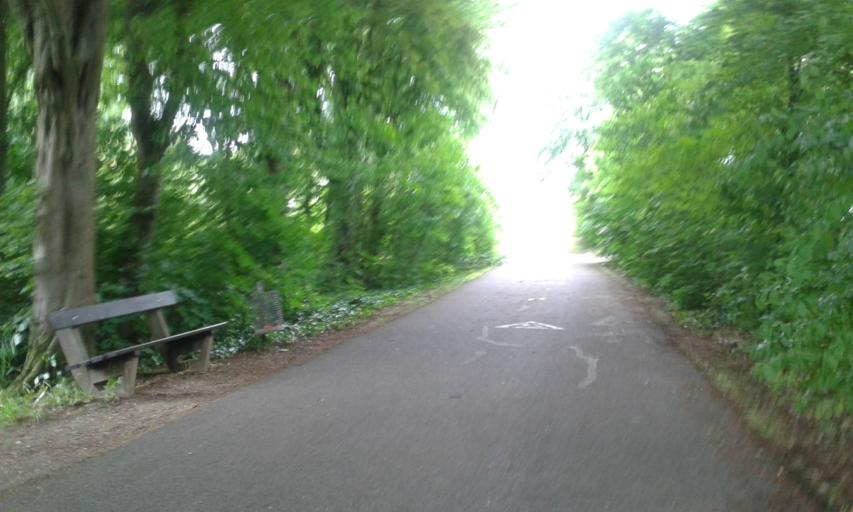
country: DE
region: Bavaria
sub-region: Regierungsbezirk Mittelfranken
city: Hersbruck
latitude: 49.5048
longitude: 11.4349
